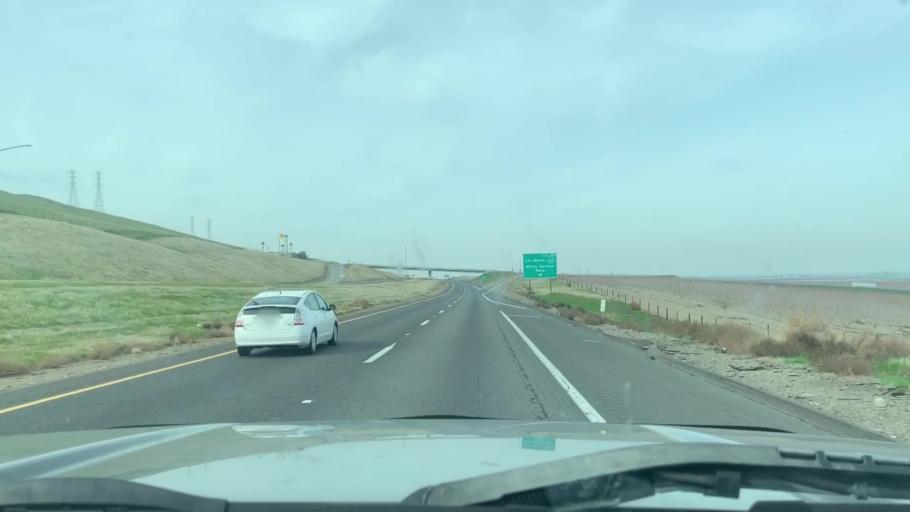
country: US
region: California
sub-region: Merced County
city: Los Banos
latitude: 36.9271
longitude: -120.8369
